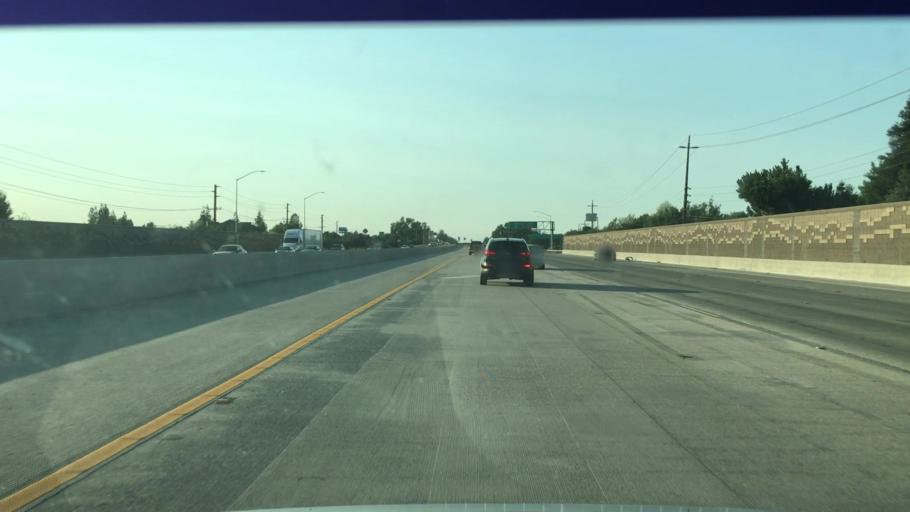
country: US
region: California
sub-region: San Joaquin County
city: Lincoln Village
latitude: 38.0163
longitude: -121.3562
